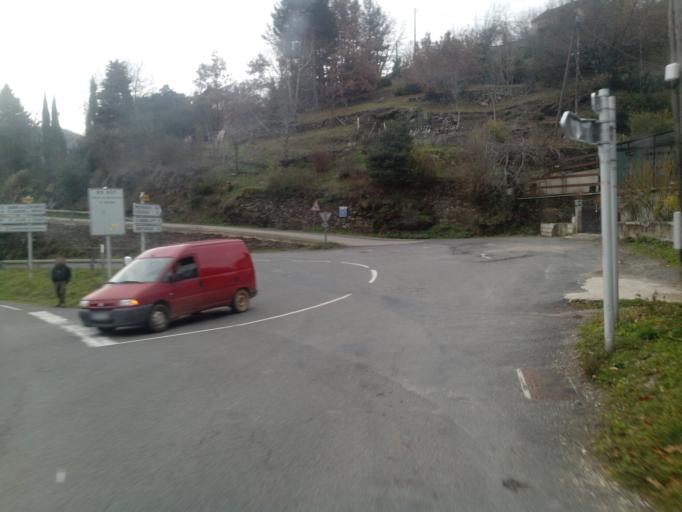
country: FR
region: Languedoc-Roussillon
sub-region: Departement de la Lozere
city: Florac
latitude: 44.2874
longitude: 3.5955
